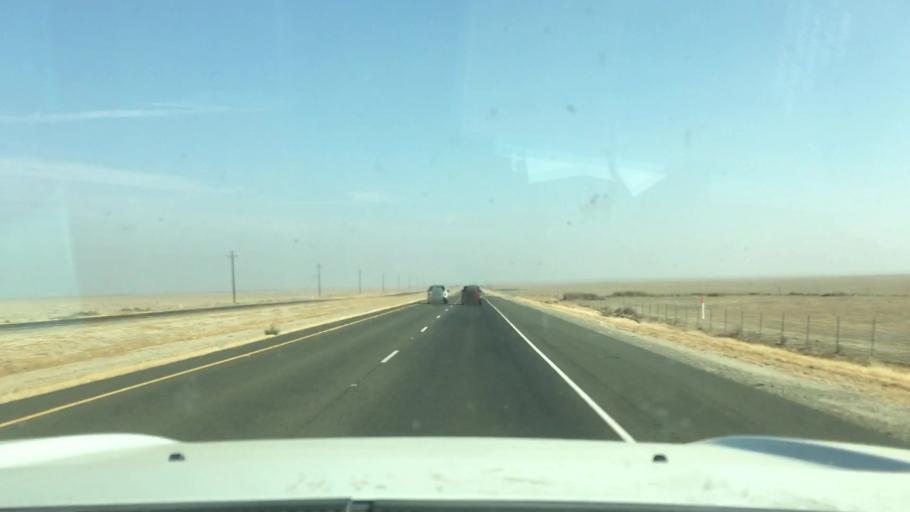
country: US
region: California
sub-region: Kern County
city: Lost Hills
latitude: 35.6153
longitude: -119.8289
